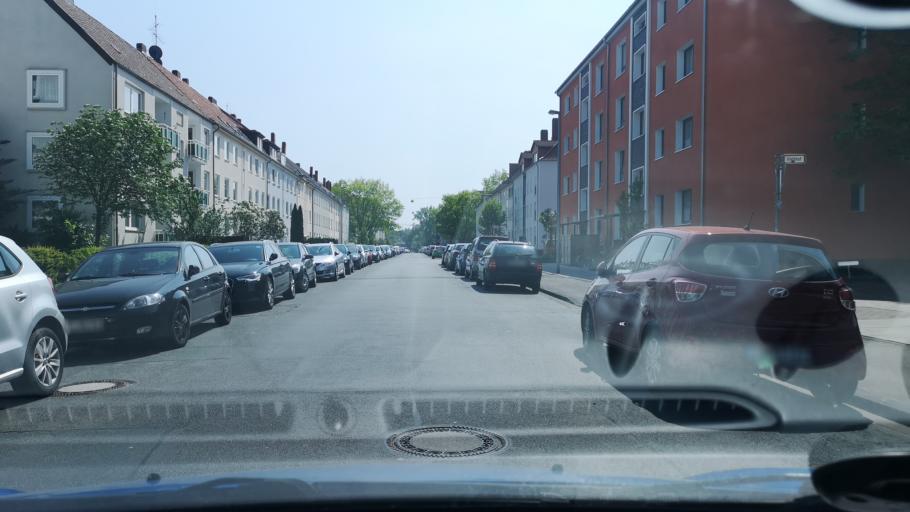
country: DE
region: Lower Saxony
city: Hannover
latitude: 52.3976
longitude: 9.7301
